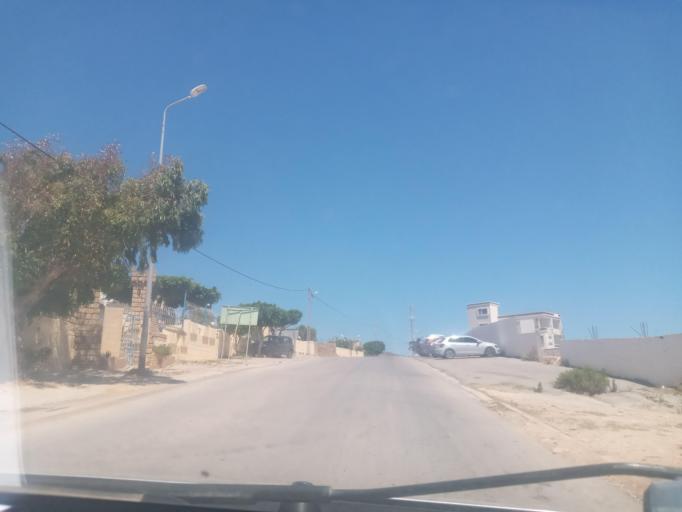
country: TN
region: Nabul
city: El Haouaria
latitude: 37.0559
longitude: 10.9987
